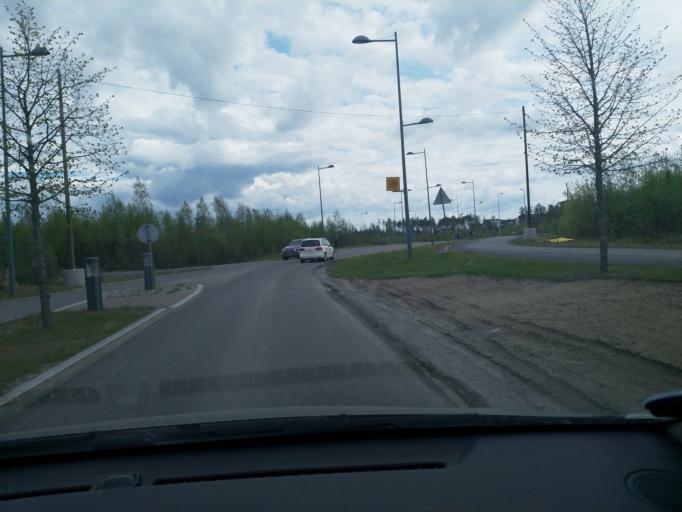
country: FI
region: Pirkanmaa
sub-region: Tampere
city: Tampere
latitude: 61.4428
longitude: 23.8073
